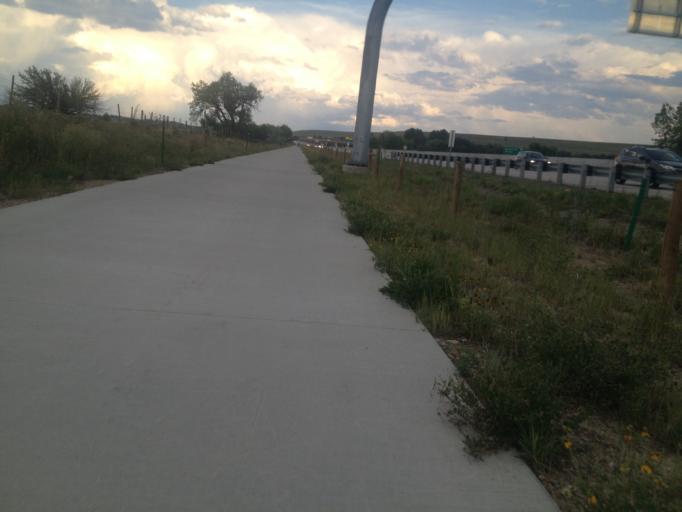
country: US
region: Colorado
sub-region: Boulder County
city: Superior
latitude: 39.9798
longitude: -105.2194
